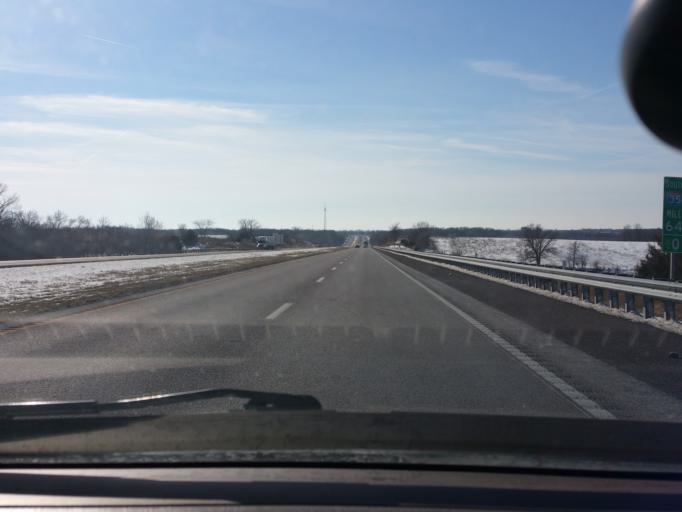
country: US
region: Missouri
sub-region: Clinton County
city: Cameron
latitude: 39.8873
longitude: -94.1586
